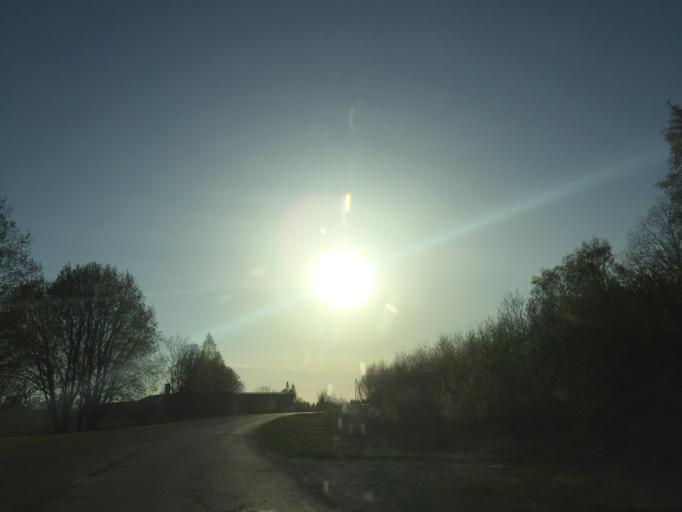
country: LV
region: Koknese
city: Koknese
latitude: 56.7251
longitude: 25.5213
